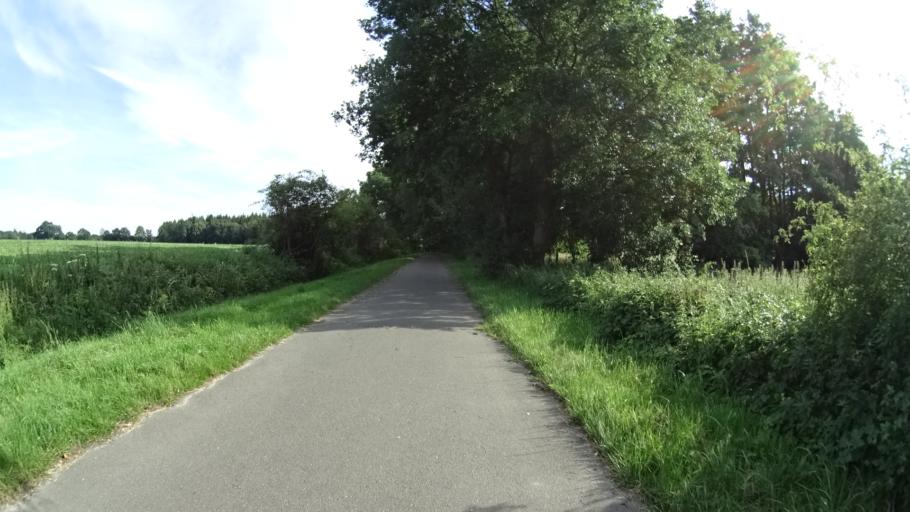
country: DE
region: Lower Saxony
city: Reppenstedt
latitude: 53.2399
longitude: 10.3584
